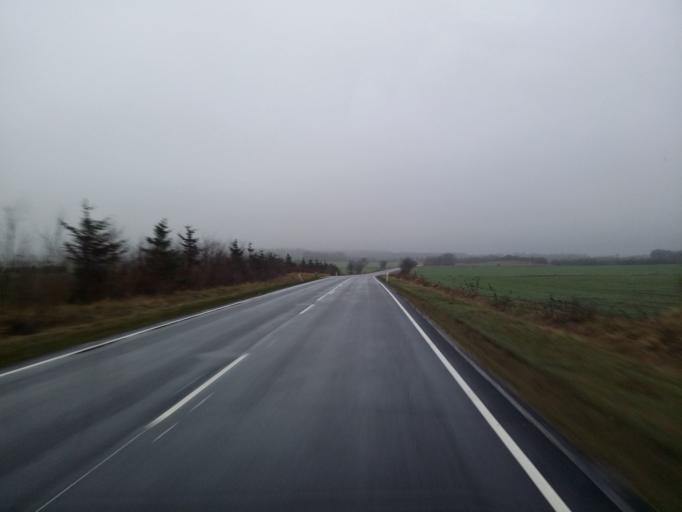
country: DK
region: Capital Region
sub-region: Frederikssund Kommune
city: Jaegerspris
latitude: 55.8226
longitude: 12.0065
